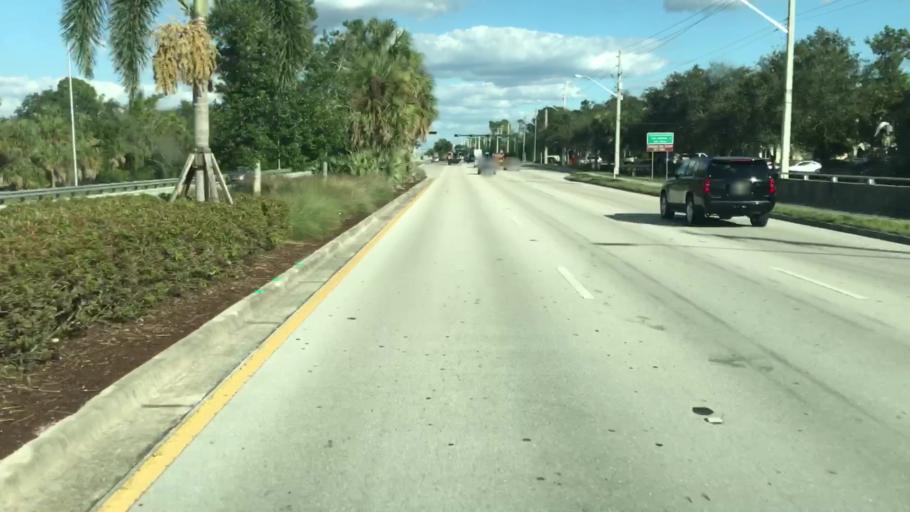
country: US
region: Florida
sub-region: Collier County
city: Naples Park
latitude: 26.2723
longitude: -81.7840
